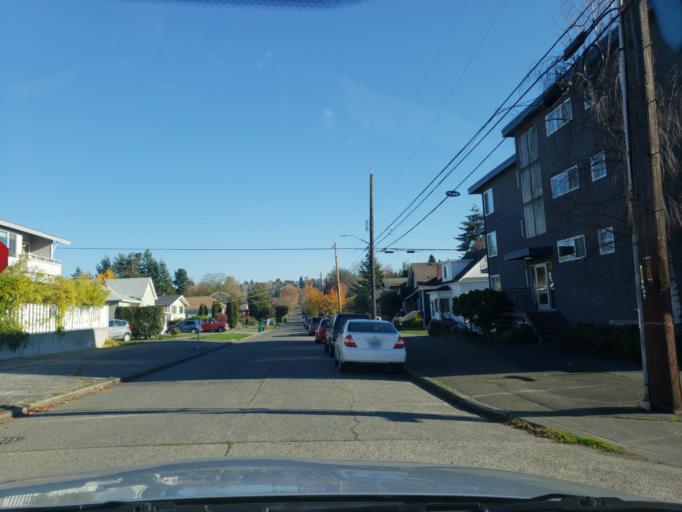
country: US
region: Washington
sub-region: King County
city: Seattle
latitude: 47.6738
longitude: -122.3735
